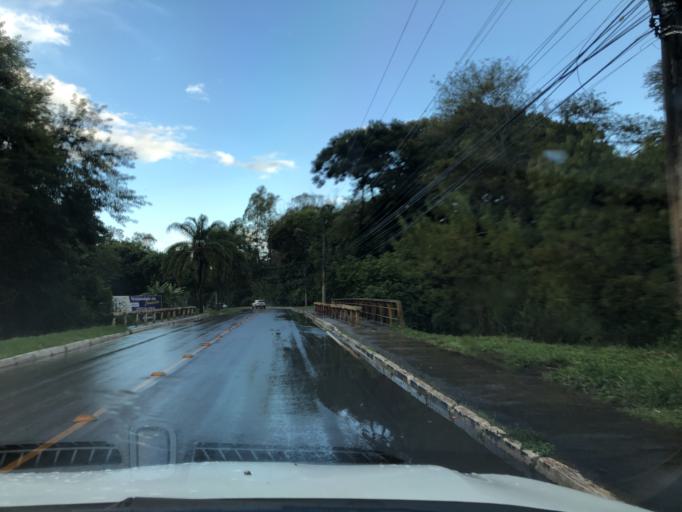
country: BR
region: Federal District
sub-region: Brasilia
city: Brasilia
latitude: -15.8748
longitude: -47.9661
